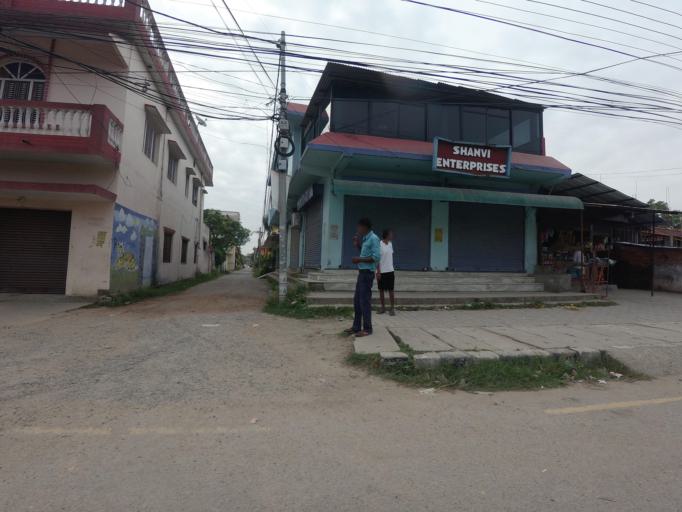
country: NP
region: Western Region
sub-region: Lumbini Zone
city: Bhairahawa
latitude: 27.4975
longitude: 83.4475
